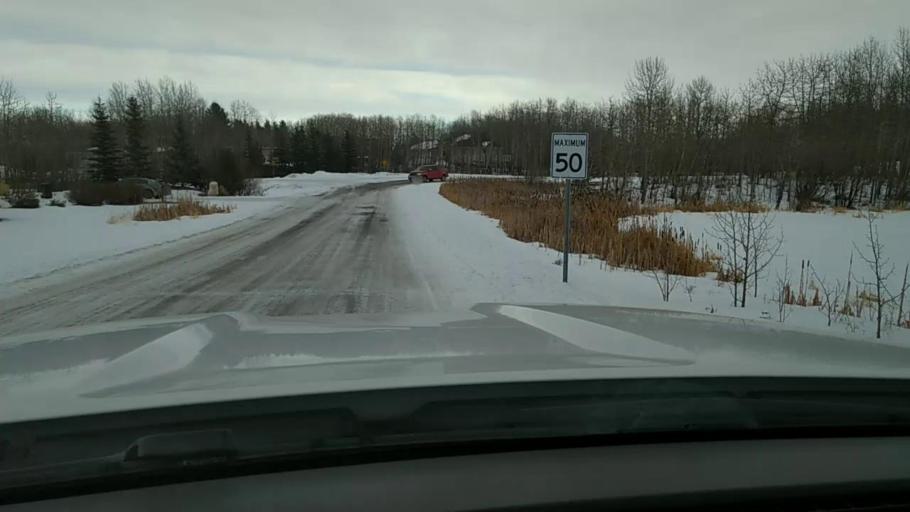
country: CA
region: Alberta
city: Cochrane
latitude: 51.1821
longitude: -114.2572
